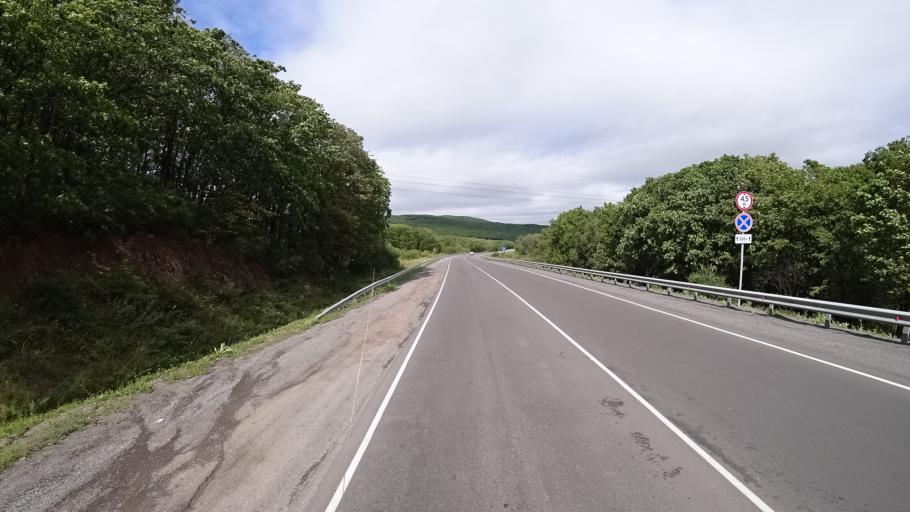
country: RU
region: Primorskiy
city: Lyalichi
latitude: 44.1322
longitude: 132.4273
